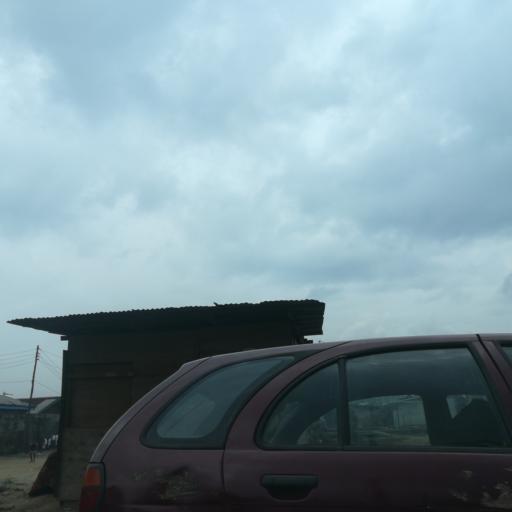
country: NG
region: Rivers
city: Port Harcourt
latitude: 4.8253
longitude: 7.0430
